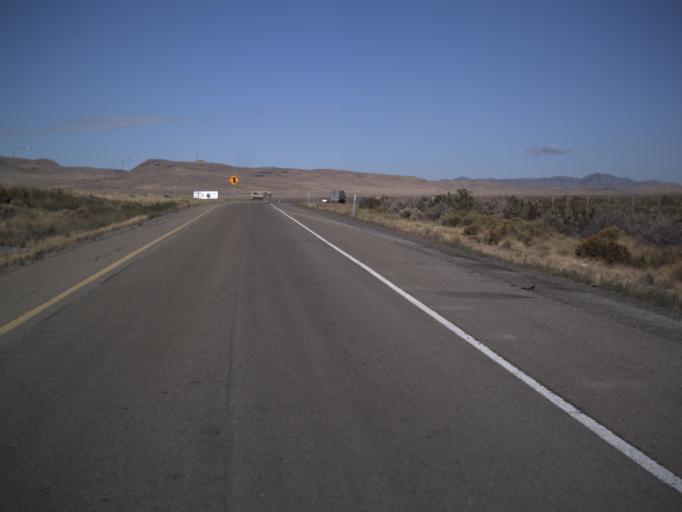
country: US
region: Utah
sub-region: Tooele County
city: Grantsville
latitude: 40.7639
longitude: -112.7821
